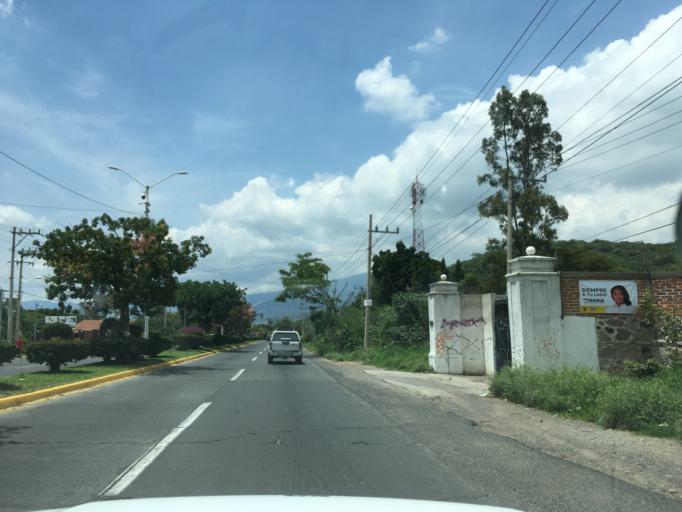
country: MX
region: Jalisco
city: Tlajomulco de Zuniga
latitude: 20.4803
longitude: -103.4546
